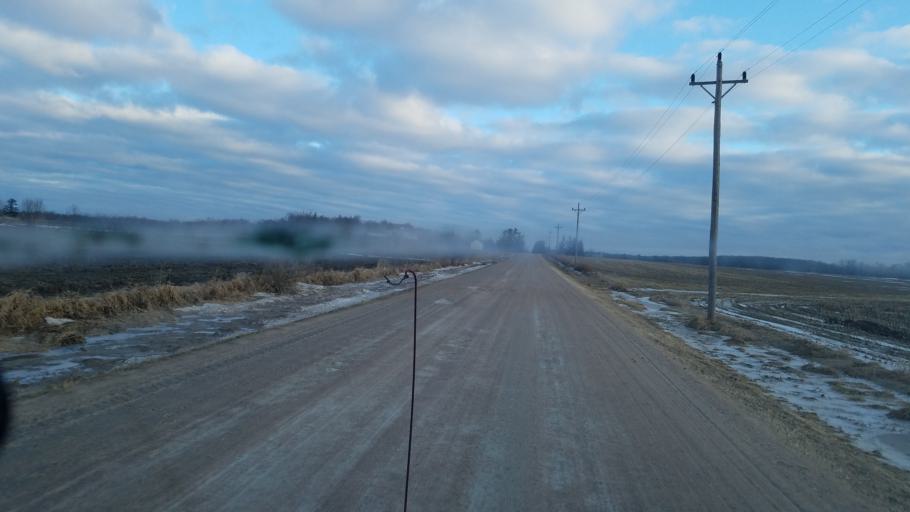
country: US
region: Wisconsin
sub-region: Clark County
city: Loyal
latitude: 44.6133
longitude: -90.4361
